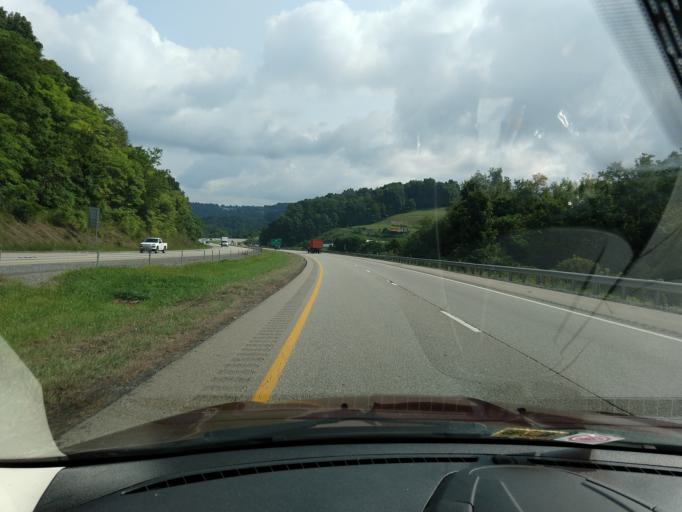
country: US
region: West Virginia
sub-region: Marion County
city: Fairmont
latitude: 39.4826
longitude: -80.0984
